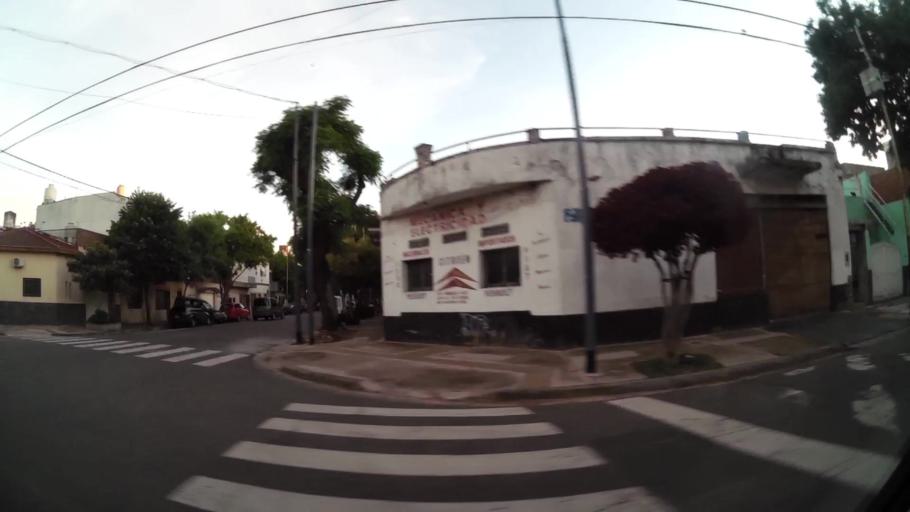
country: AR
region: Buenos Aires F.D.
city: Villa Santa Rita
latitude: -34.6397
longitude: -58.4341
